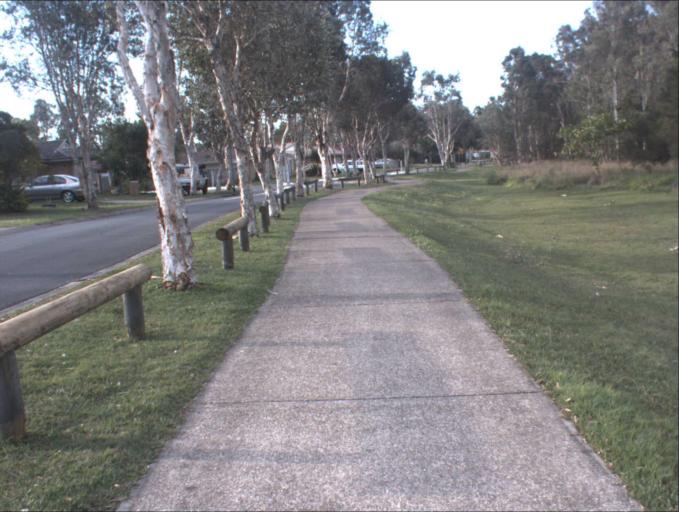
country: AU
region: Queensland
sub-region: Logan
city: Logan Reserve
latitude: -27.6968
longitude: 153.0877
